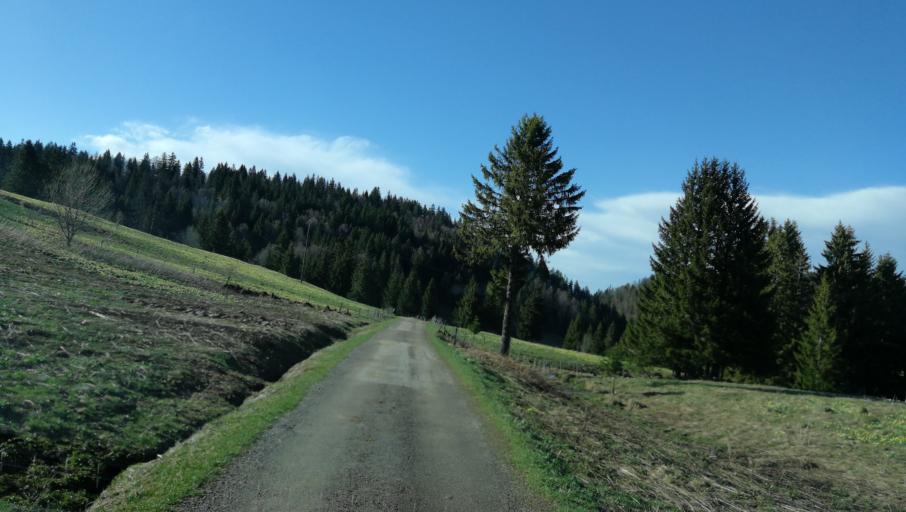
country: FR
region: Franche-Comte
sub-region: Departement du Jura
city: Saint-Claude
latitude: 46.2995
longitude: 5.8631
